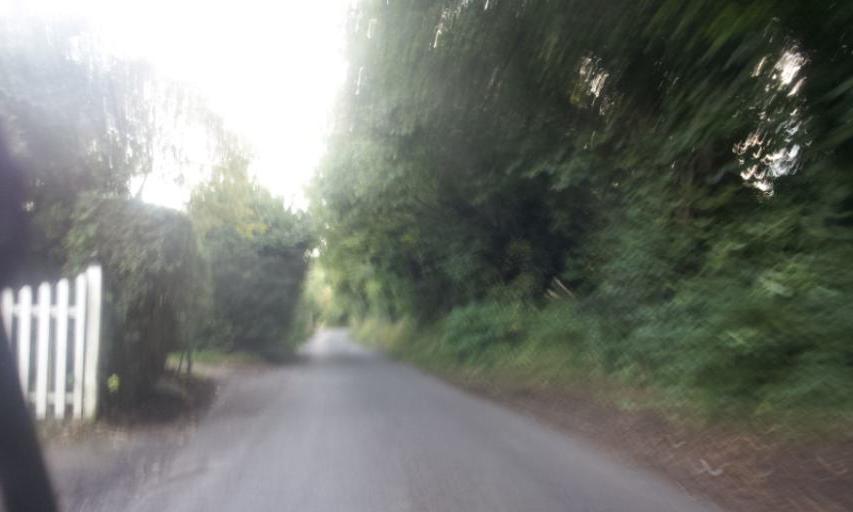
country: GB
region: England
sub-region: Kent
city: Meopham
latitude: 51.3781
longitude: 0.3967
